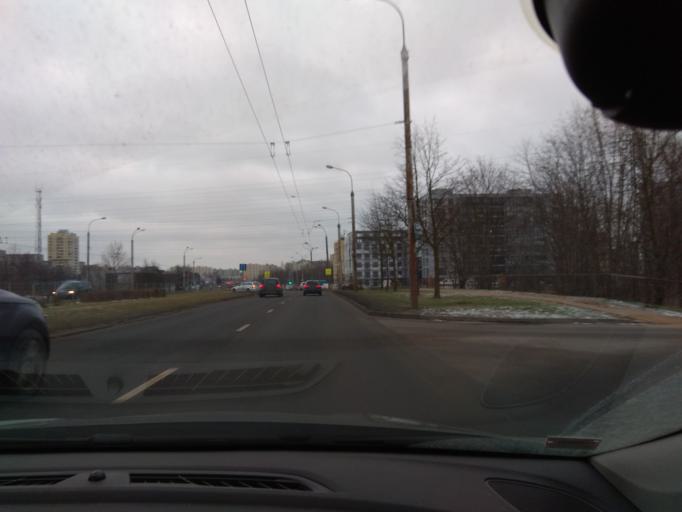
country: LT
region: Vilnius County
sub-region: Vilnius
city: Fabijoniskes
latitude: 54.7209
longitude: 25.2335
